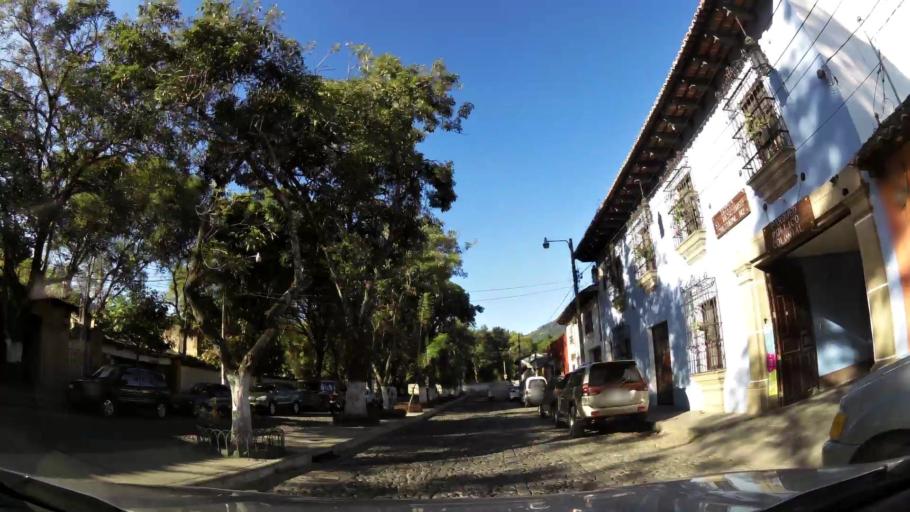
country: GT
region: Sacatepequez
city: Antigua Guatemala
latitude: 14.5600
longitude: -90.7378
